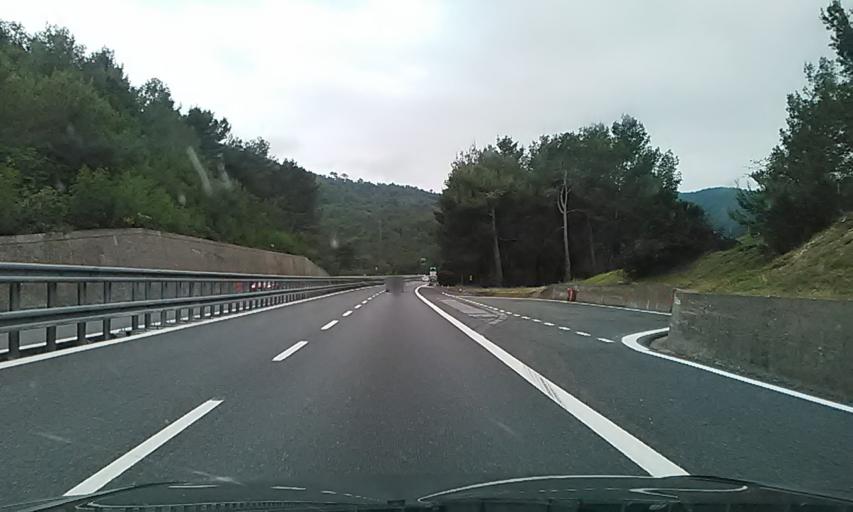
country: IT
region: Liguria
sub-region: Provincia di Savona
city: Villanova d'Albenga
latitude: 44.0346
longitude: 8.1335
